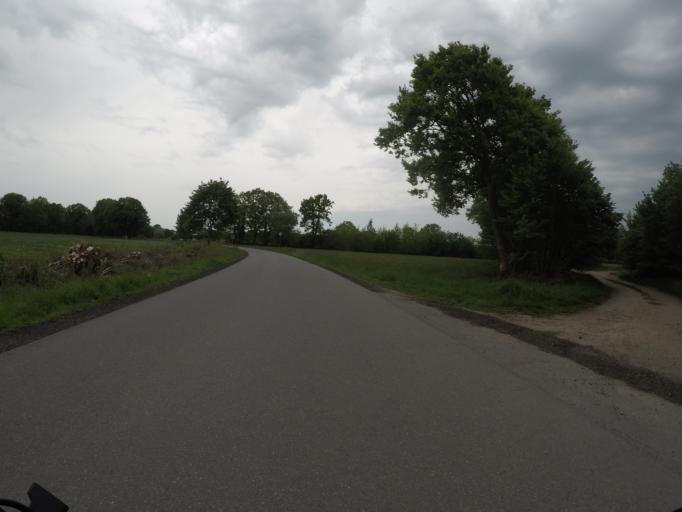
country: DE
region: Schleswig-Holstein
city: Kisdorf
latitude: 53.7818
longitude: 10.0214
